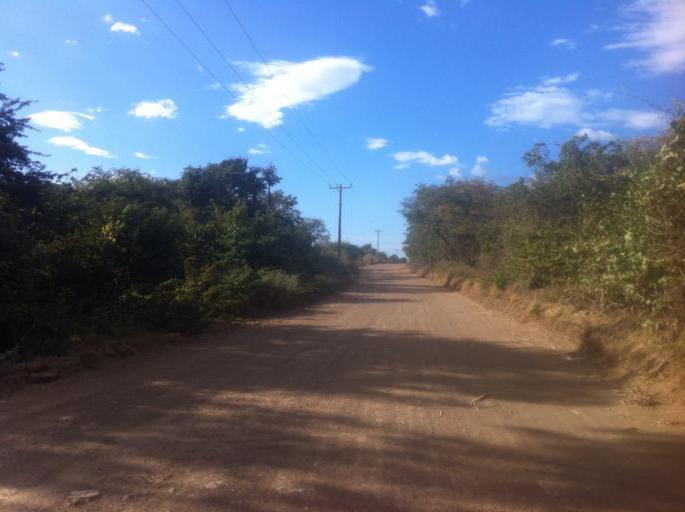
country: NI
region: Managua
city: Masachapa
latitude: 11.8129
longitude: -86.4958
